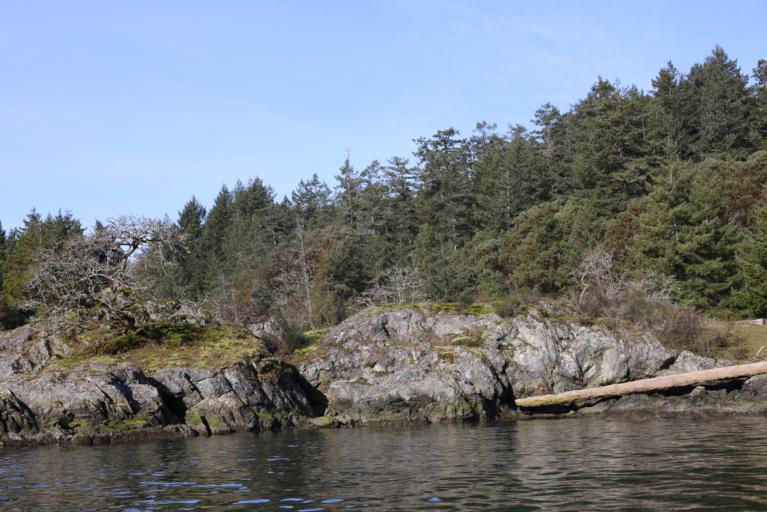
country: CA
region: British Columbia
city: Duncan
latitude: 48.7526
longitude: -123.5817
